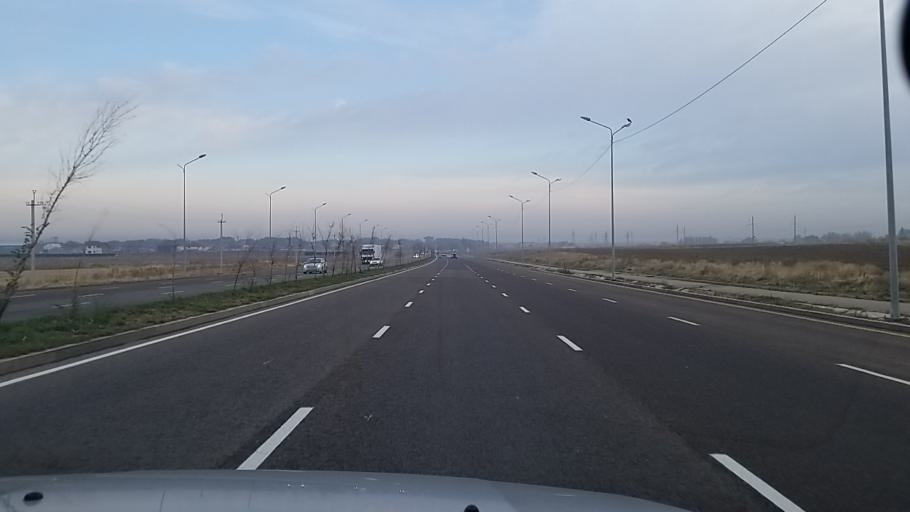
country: KZ
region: Almaty Oblysy
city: Burunday
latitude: 43.3434
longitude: 76.8338
